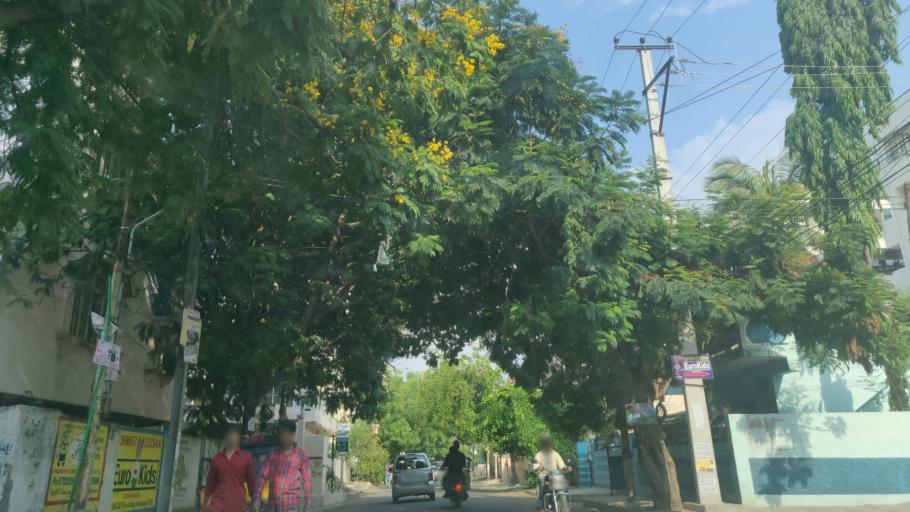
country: IN
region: Telangana
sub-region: Rangareddi
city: Gaddi Annaram
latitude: 17.3758
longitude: 78.5182
